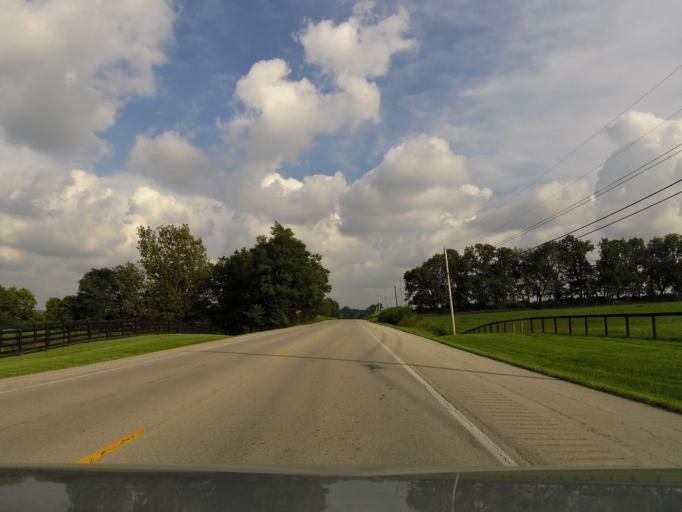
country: US
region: Kentucky
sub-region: Bourbon County
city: Paris
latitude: 38.2466
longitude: -84.2865
